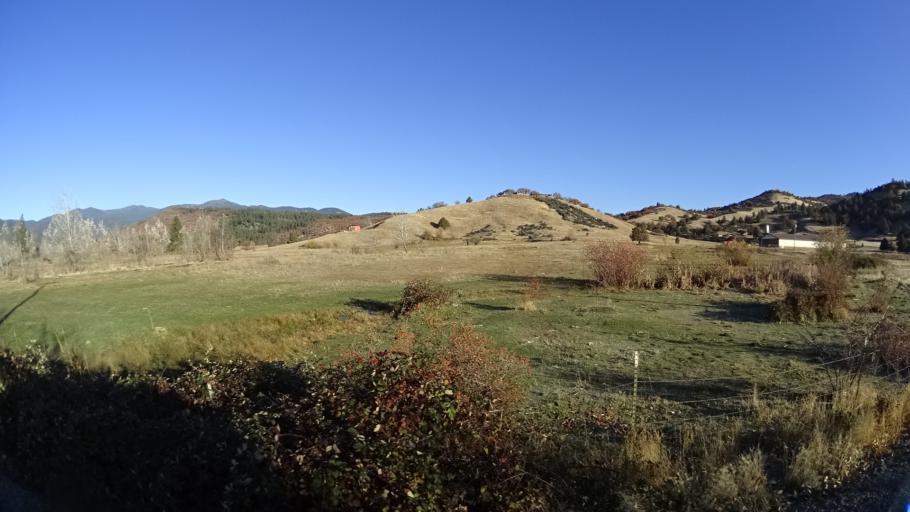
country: US
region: Oregon
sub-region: Jackson County
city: Ashland
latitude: 41.9958
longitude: -122.6229
